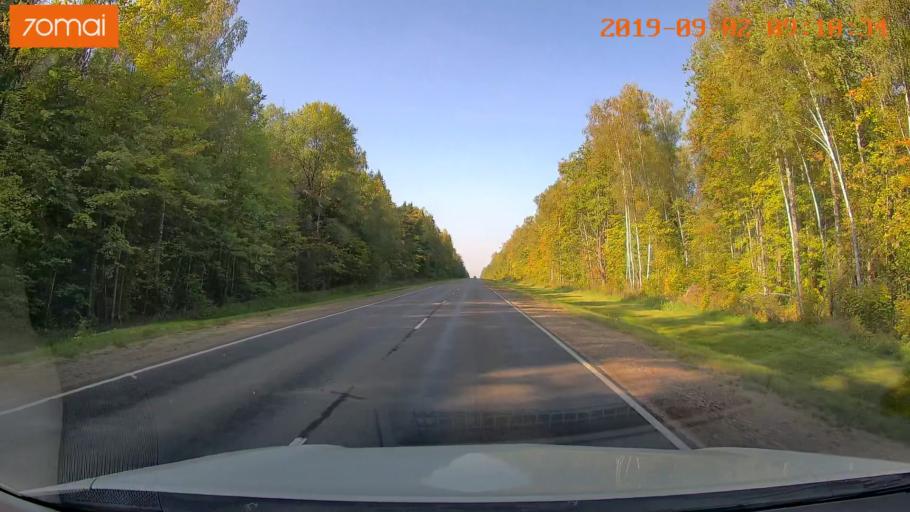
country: RU
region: Kaluga
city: Myatlevo
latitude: 54.8748
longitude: 35.5970
